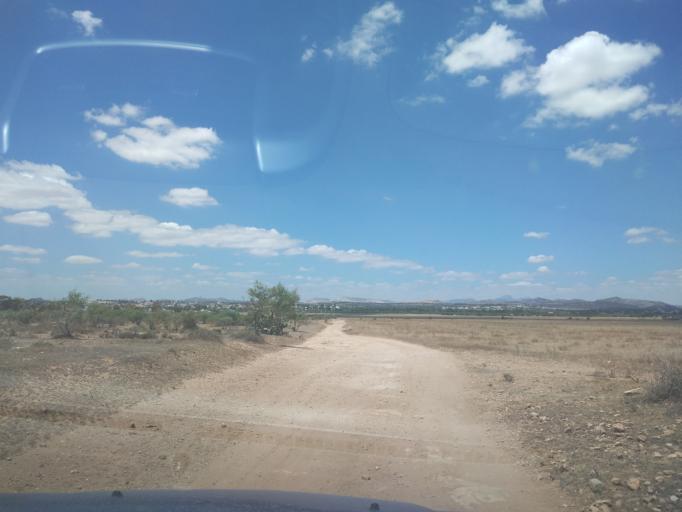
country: TN
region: Susah
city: Harqalah
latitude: 36.1673
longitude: 10.4385
